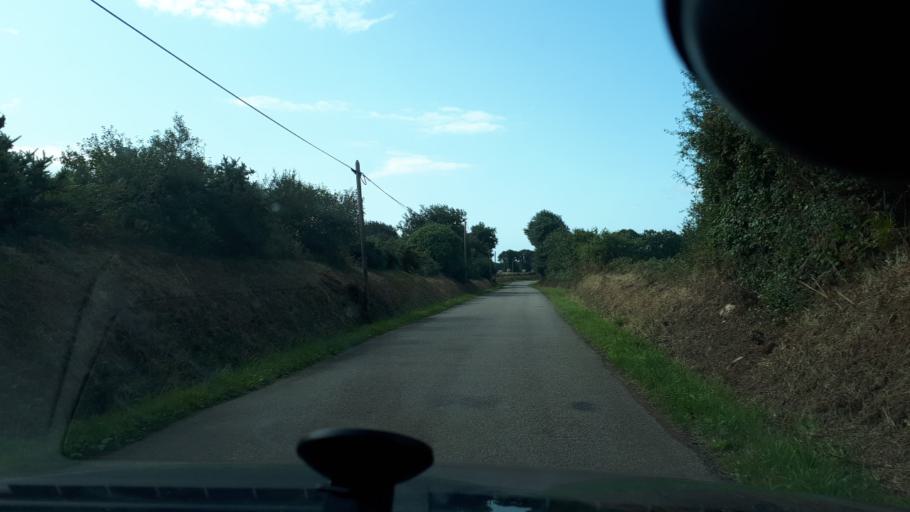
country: FR
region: Brittany
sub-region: Departement du Finistere
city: Landudec
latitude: 47.9960
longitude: -4.3644
